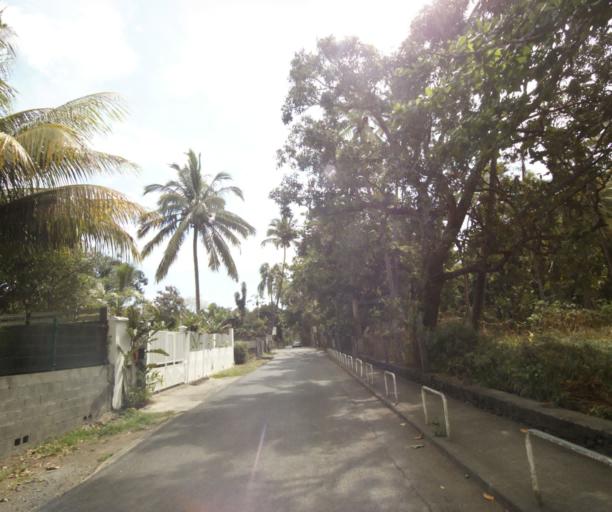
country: RE
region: Reunion
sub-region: Reunion
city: Saint-Paul
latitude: -21.0111
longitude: 55.2818
